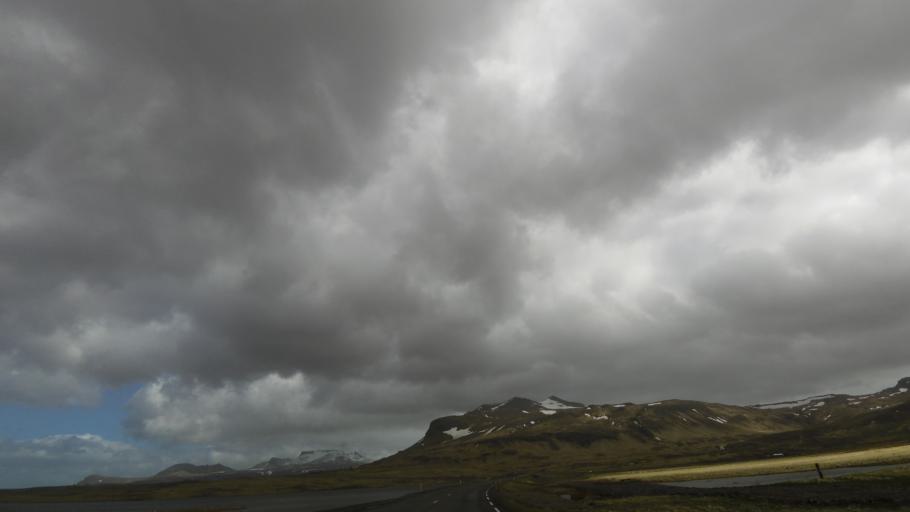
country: IS
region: West
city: Olafsvik
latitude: 64.8918
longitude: -23.6205
